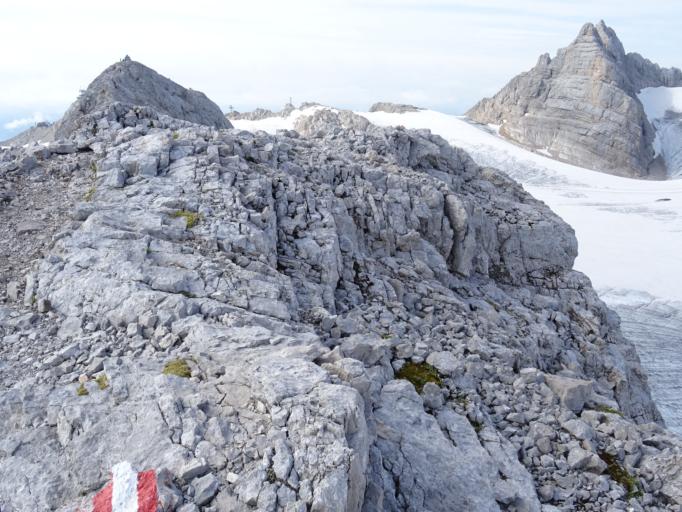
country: AT
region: Styria
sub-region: Politischer Bezirk Liezen
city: Schladming
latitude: 47.4786
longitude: 13.6301
